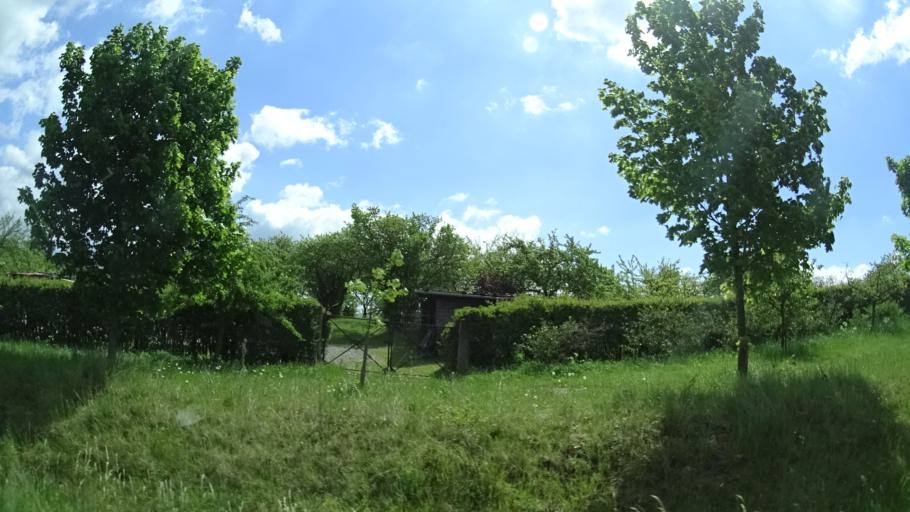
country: DE
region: Thuringia
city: Marisfeld
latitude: 50.5534
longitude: 10.5611
